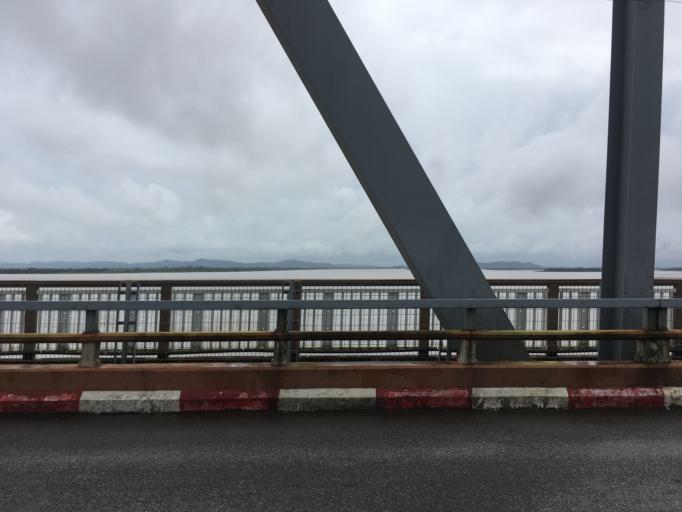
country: MM
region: Mon
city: Mawlamyine
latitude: 16.5060
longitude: 97.6203
